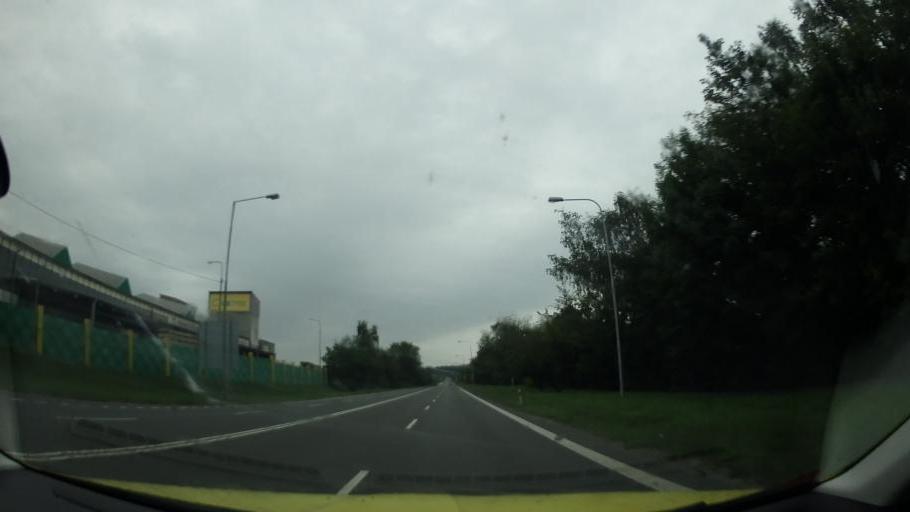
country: CZ
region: Olomoucky
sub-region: Okres Prerov
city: Hranice
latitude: 49.5590
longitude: 17.7519
